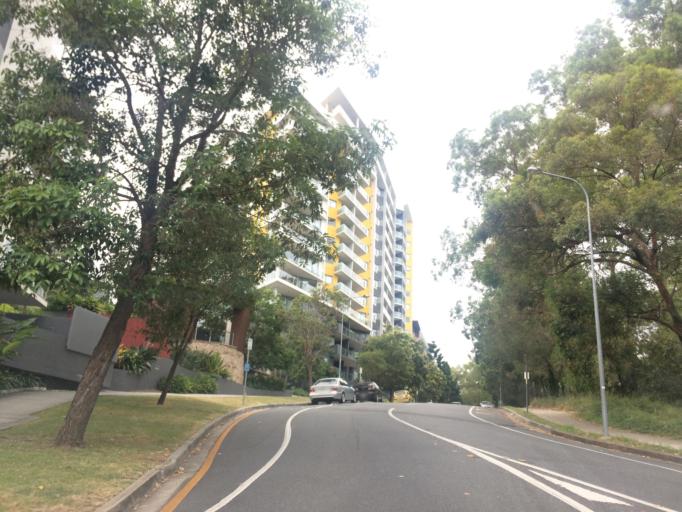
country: AU
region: Queensland
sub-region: Brisbane
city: Spring Hill
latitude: -27.4542
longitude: 153.0160
